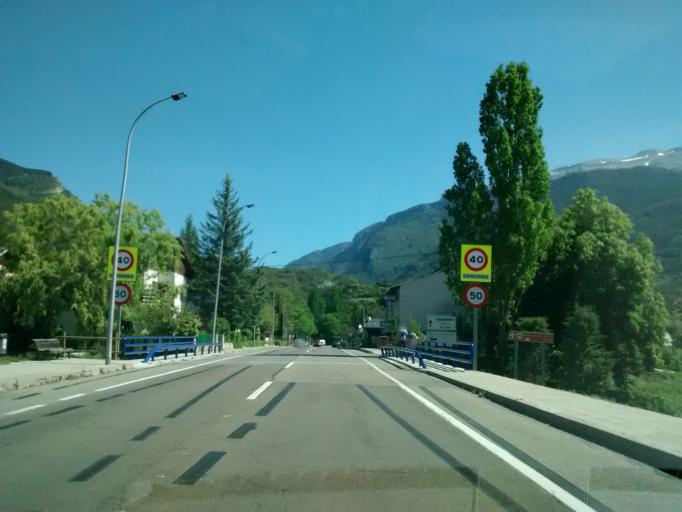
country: ES
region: Aragon
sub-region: Provincia de Huesca
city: Villanua
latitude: 42.6800
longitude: -0.5368
